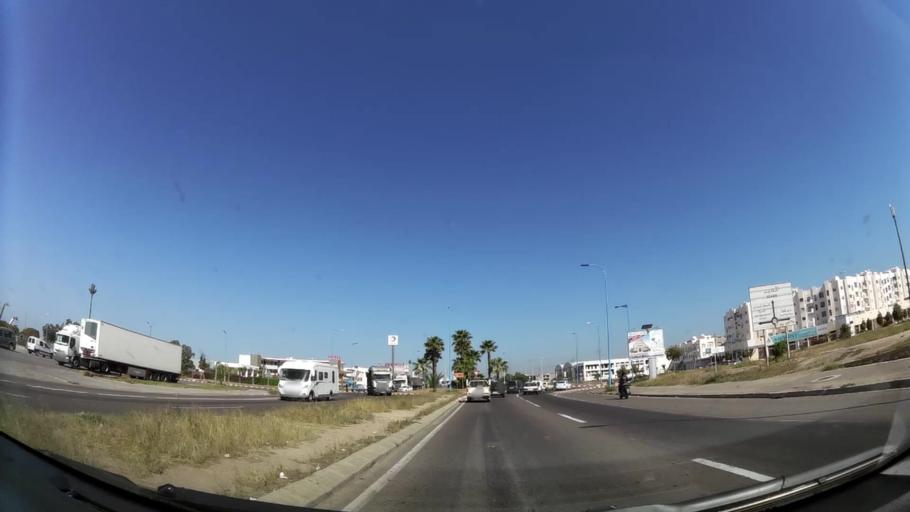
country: MA
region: Oued ed Dahab-Lagouira
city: Dakhla
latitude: 30.3965
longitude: -9.5223
